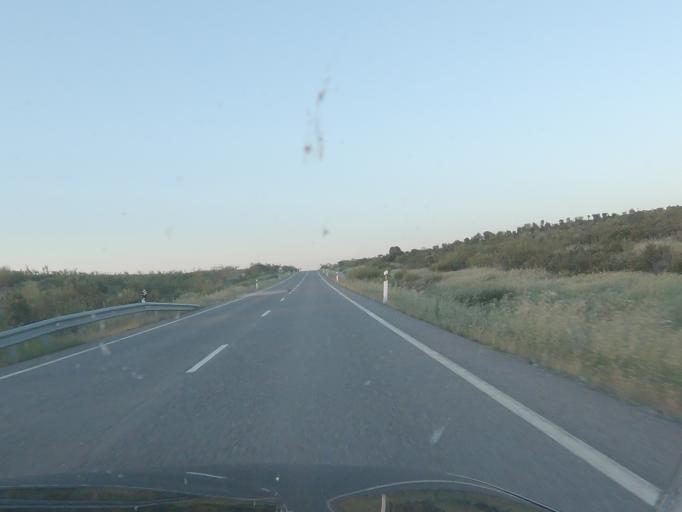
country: ES
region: Extremadura
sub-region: Provincia de Caceres
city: Salorino
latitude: 39.5997
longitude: -6.9810
